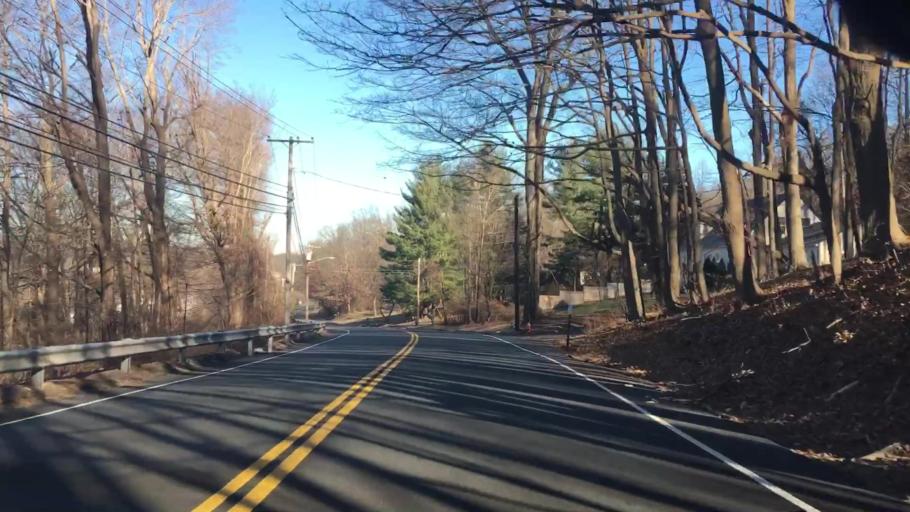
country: US
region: Connecticut
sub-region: New Haven County
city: Meriden
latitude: 41.5350
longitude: -72.7521
